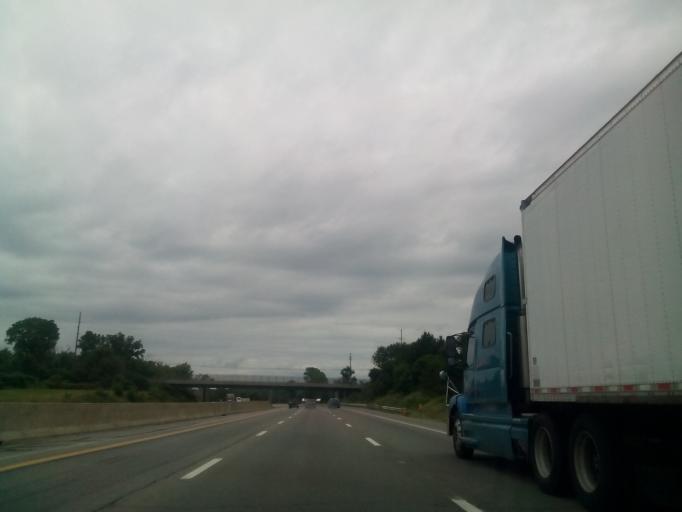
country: US
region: Ohio
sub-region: Huron County
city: Wakeman
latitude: 41.3344
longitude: -82.3762
